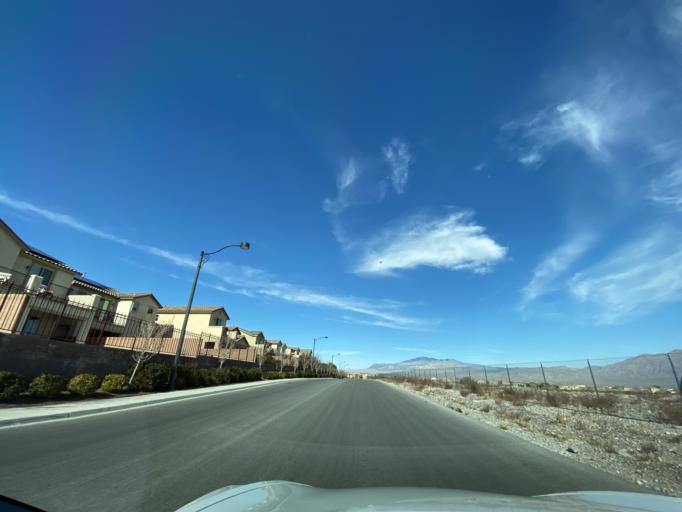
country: US
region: Nevada
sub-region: Clark County
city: Summerlin South
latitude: 36.2963
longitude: -115.3265
